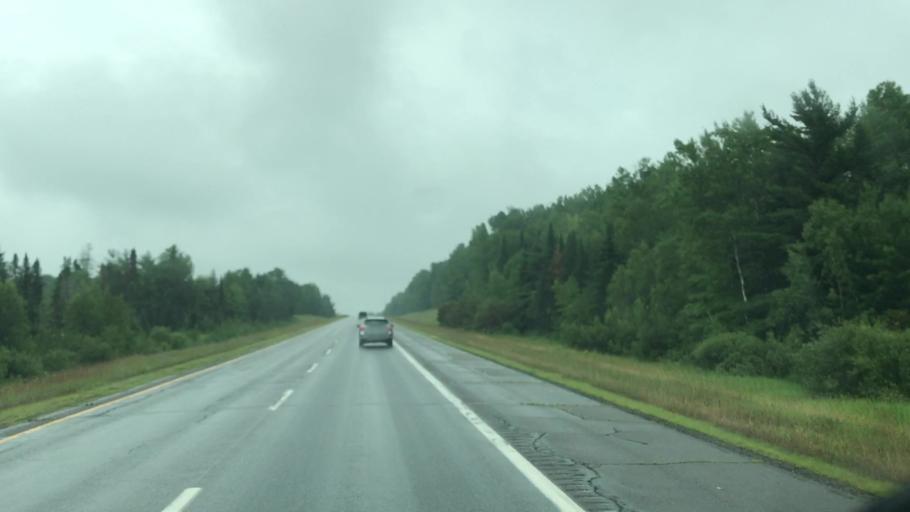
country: US
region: Maine
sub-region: Penobscot County
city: Howland
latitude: 45.2043
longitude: -68.6823
